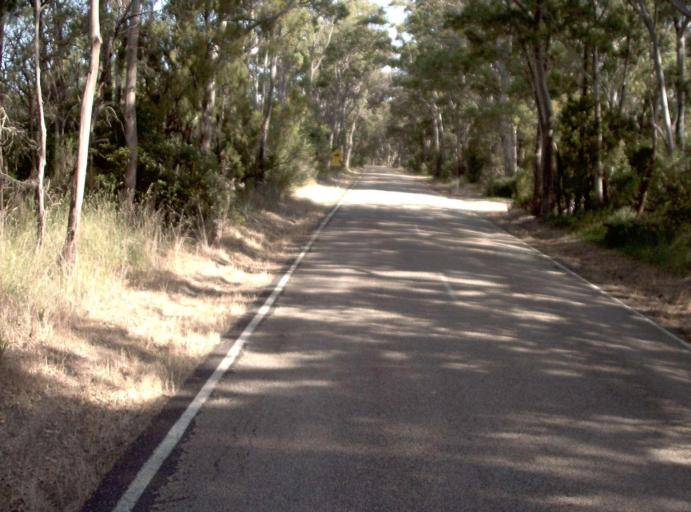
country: AU
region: Victoria
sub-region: East Gippsland
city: Lakes Entrance
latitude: -37.7889
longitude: 147.8296
